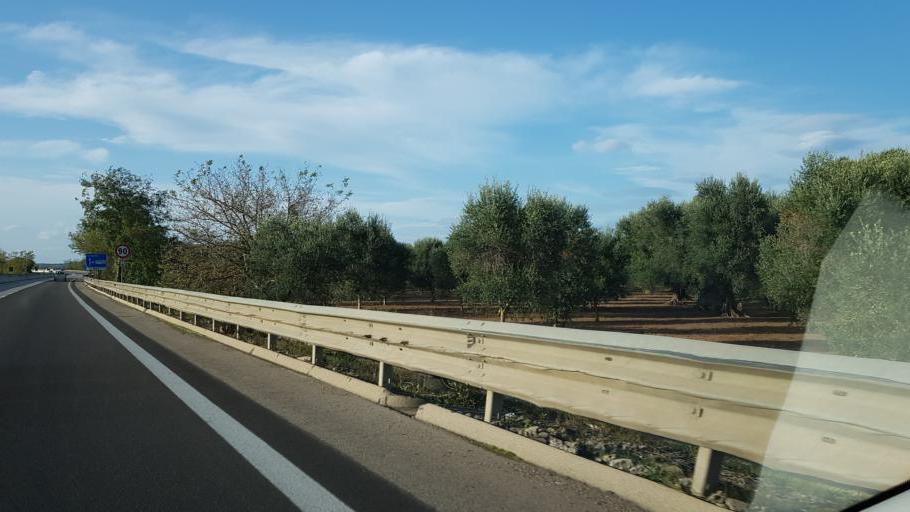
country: IT
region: Apulia
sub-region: Provincia di Brindisi
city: Francavilla Fontana
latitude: 40.5426
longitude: 17.6007
